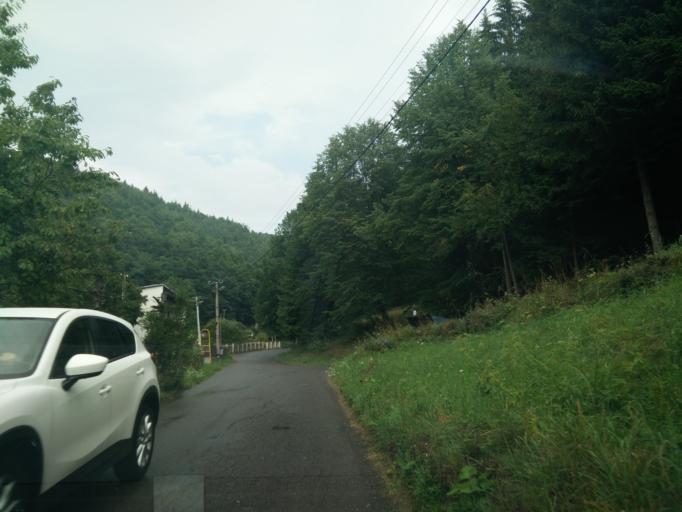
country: SK
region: Banskobystricky
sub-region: Okres Banska Bystrica
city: Banska Stiavnica
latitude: 48.4868
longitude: 18.8629
